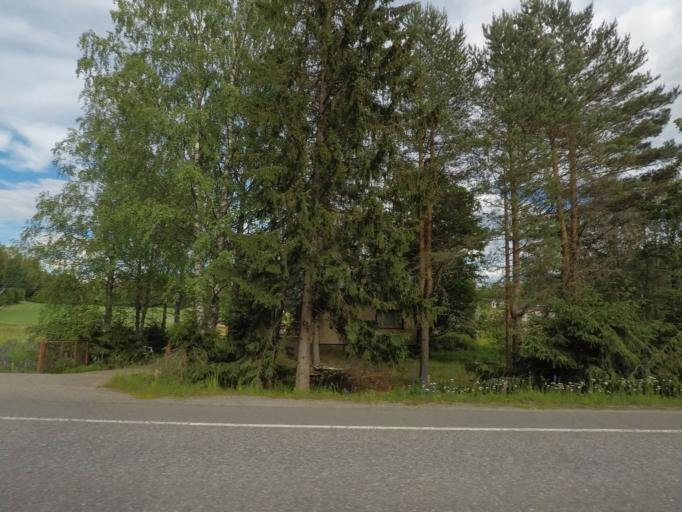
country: FI
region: Paijanne Tavastia
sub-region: Lahti
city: Hollola
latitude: 60.8711
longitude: 25.5020
